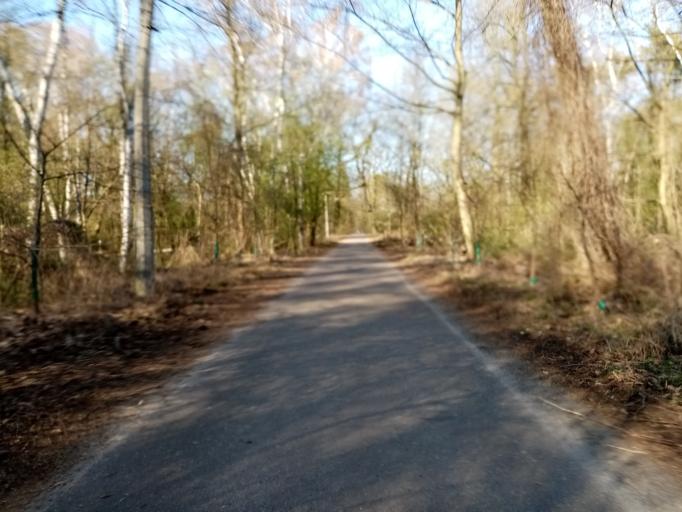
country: DE
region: Berlin
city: Oberschoneweide
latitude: 52.4652
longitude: 13.5418
